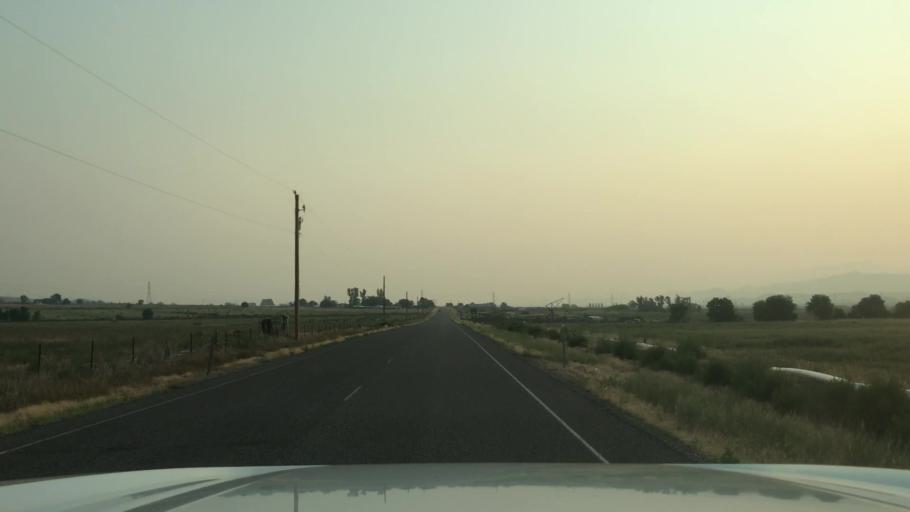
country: US
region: Utah
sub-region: Sevier County
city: Aurora
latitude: 38.8826
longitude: -111.9605
